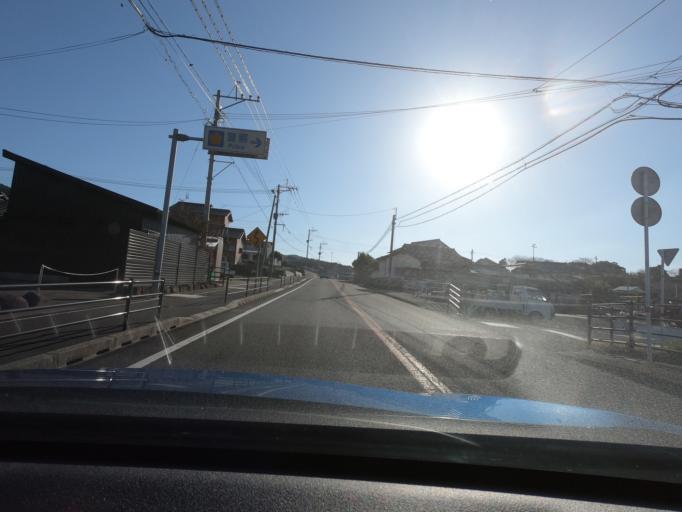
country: JP
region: Kumamoto
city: Minamata
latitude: 32.1746
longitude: 130.3828
